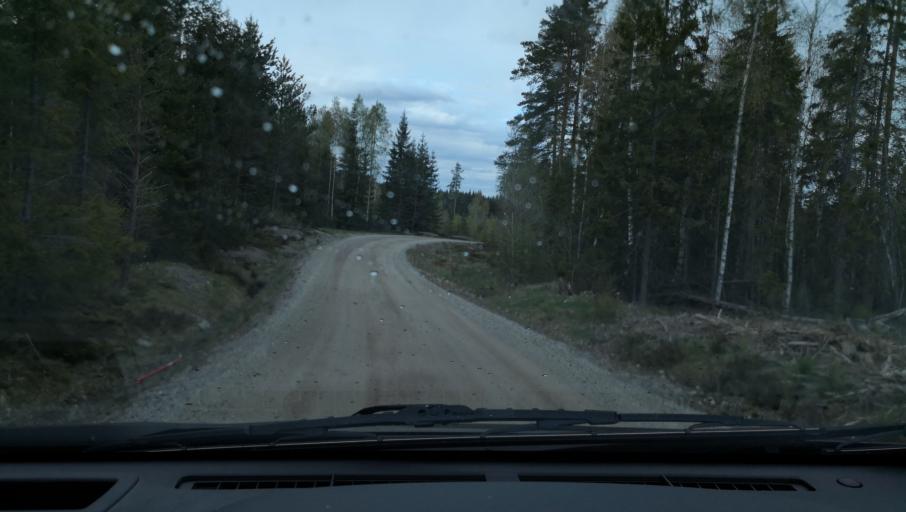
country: SE
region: Dalarna
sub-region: Saters Kommun
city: Saeter
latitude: 60.2004
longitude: 15.7456
